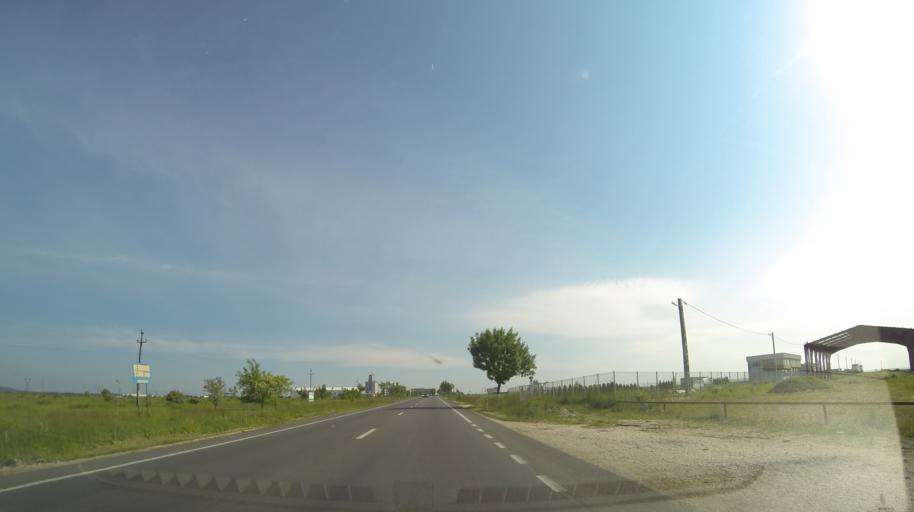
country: RO
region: Arges
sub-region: Comuna Bradu
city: Geamana
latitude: 44.8020
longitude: 24.8634
